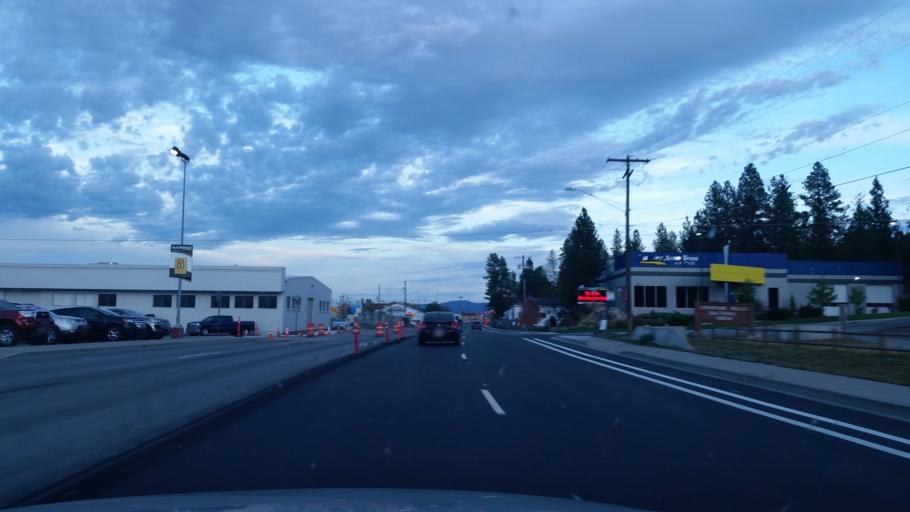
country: US
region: Washington
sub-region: Spokane County
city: Dishman
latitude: 47.6554
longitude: -117.2897
